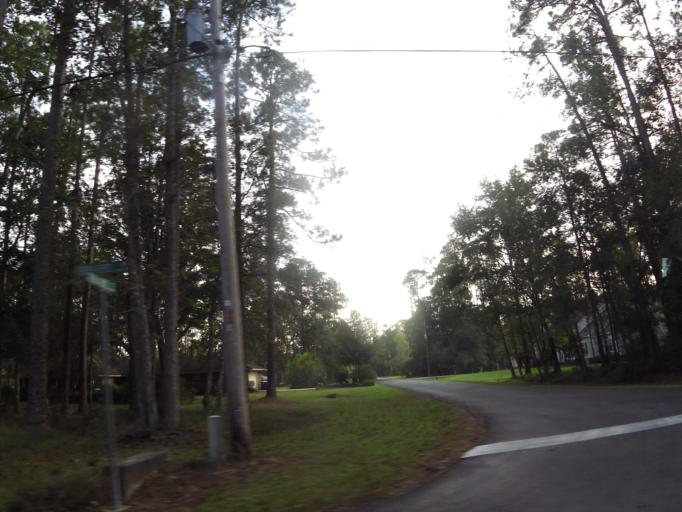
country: US
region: Florida
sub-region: Saint Johns County
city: Fruit Cove
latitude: 30.1577
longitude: -81.5714
